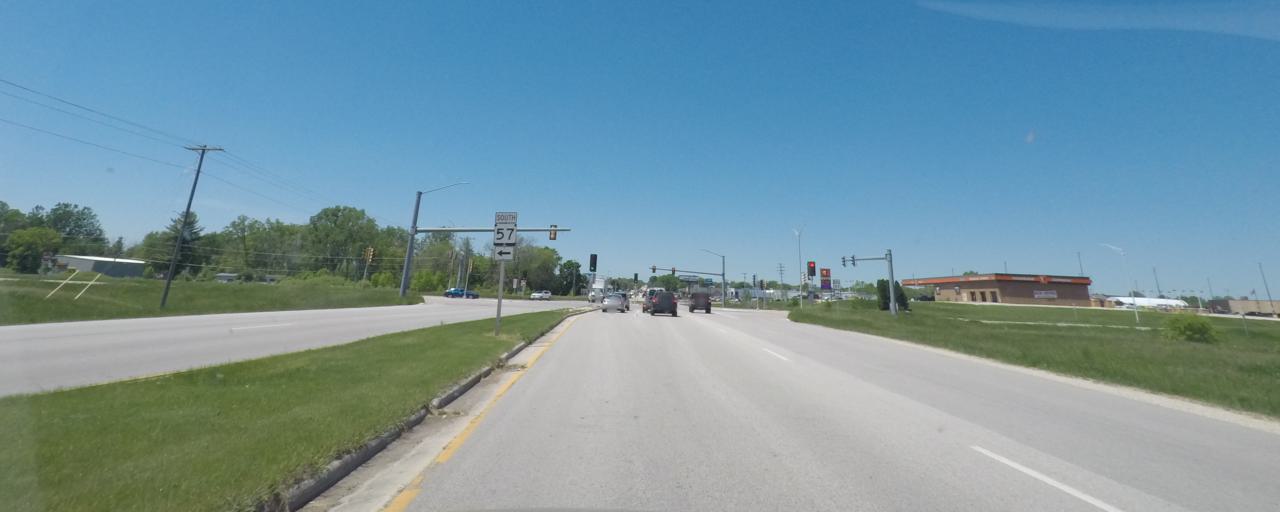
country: US
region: Wisconsin
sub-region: Sheboygan County
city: Plymouth
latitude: 43.7472
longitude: -87.9400
